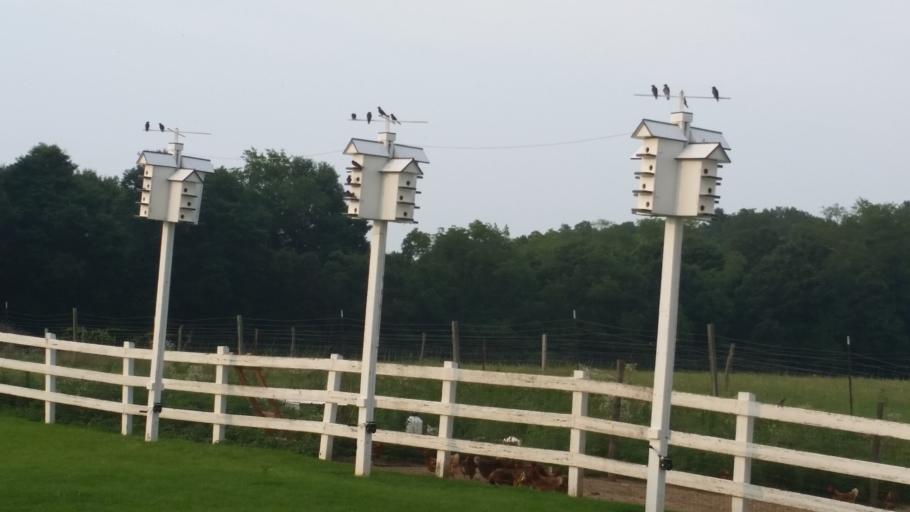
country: US
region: Ohio
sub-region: Gallia County
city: Gallipolis
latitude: 38.8306
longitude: -82.3207
